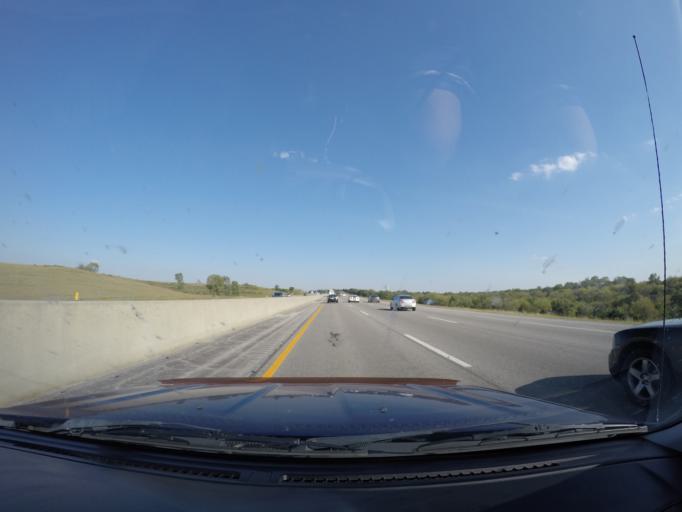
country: US
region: Kansas
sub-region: Shawnee County
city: Topeka
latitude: 39.0206
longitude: -95.5335
